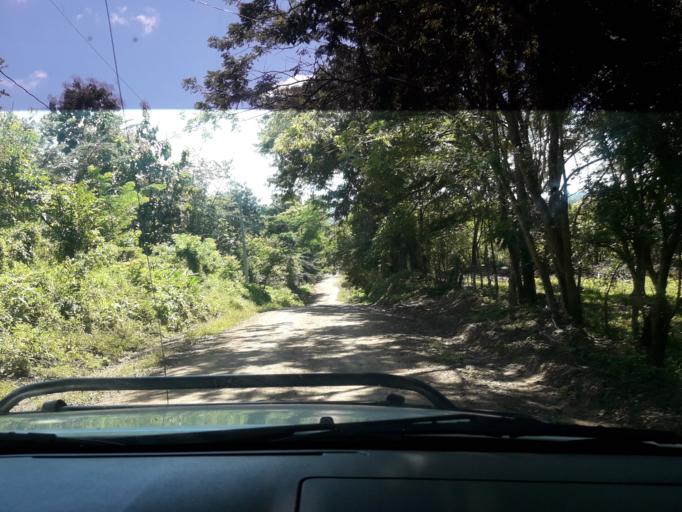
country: NI
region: Rivas
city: Cardenas
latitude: 11.2264
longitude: -85.6493
